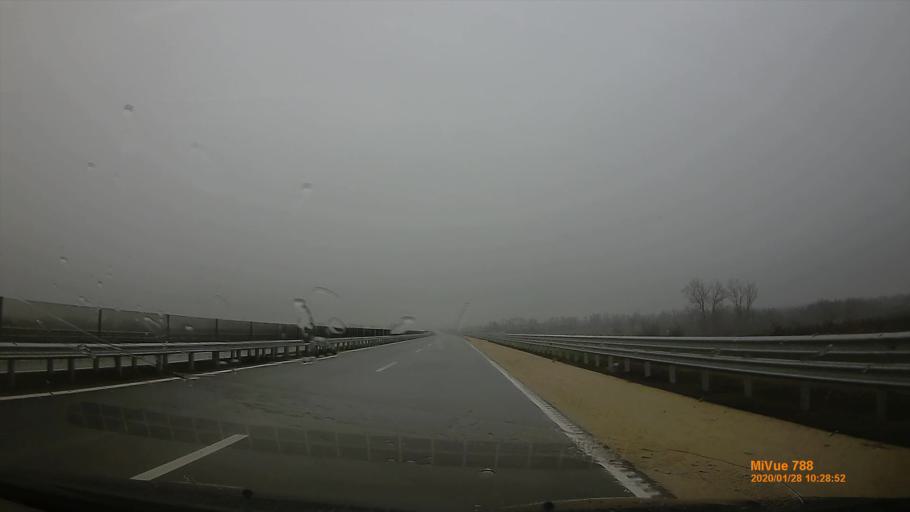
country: HU
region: Pest
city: Pilis
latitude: 47.3203
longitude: 19.5424
